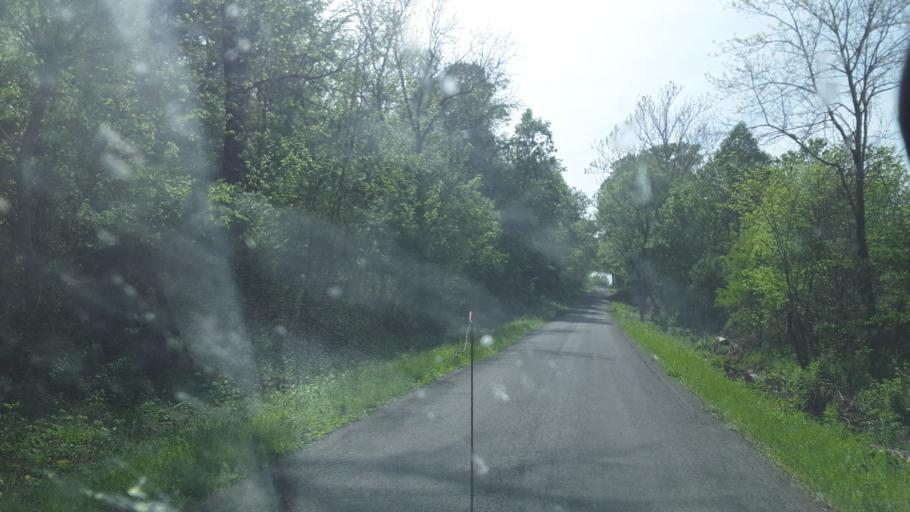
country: US
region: Illinois
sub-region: Jackson County
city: Carbondale
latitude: 37.6808
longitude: -89.2891
